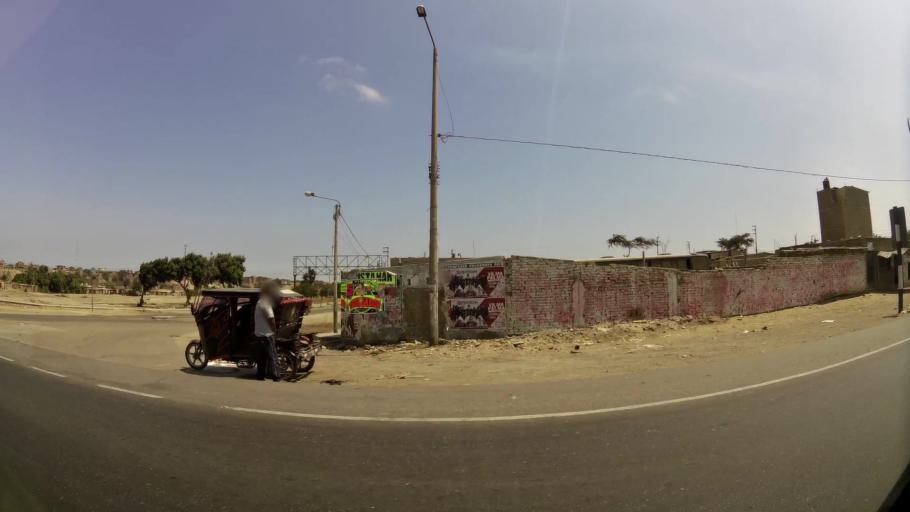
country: PE
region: La Libertad
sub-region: Provincia de Pacasmayo
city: Pacasmayo
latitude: -7.3998
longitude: -79.5587
